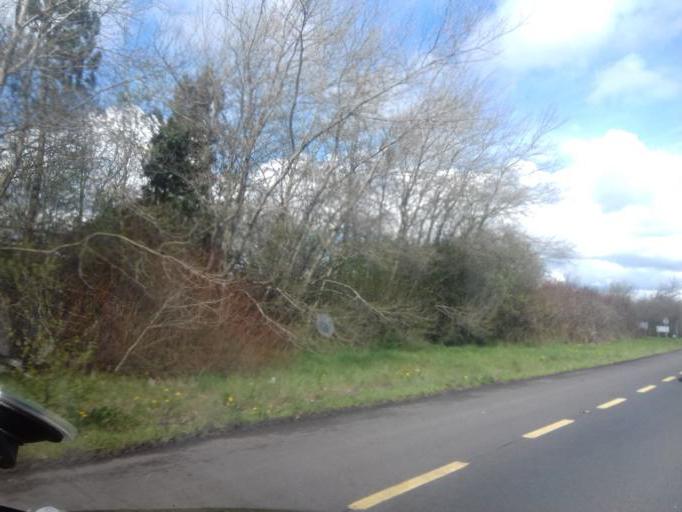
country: IE
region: Ulster
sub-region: An Cabhan
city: Belturbet
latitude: 54.1119
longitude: -7.4715
